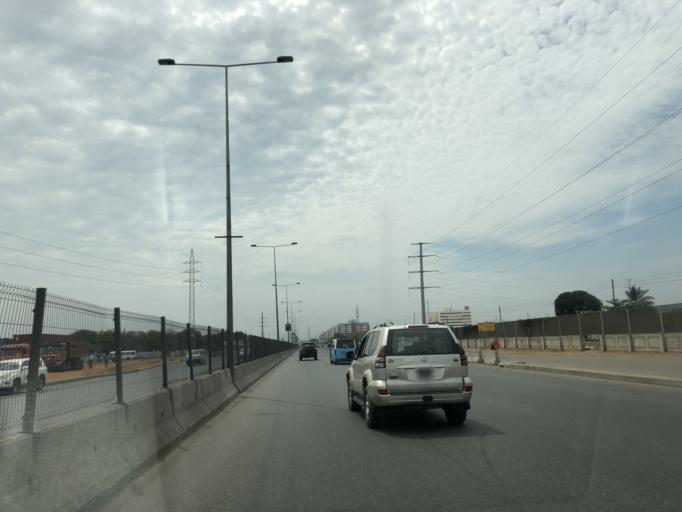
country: AO
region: Luanda
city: Luanda
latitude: -8.8573
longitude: 13.2987
